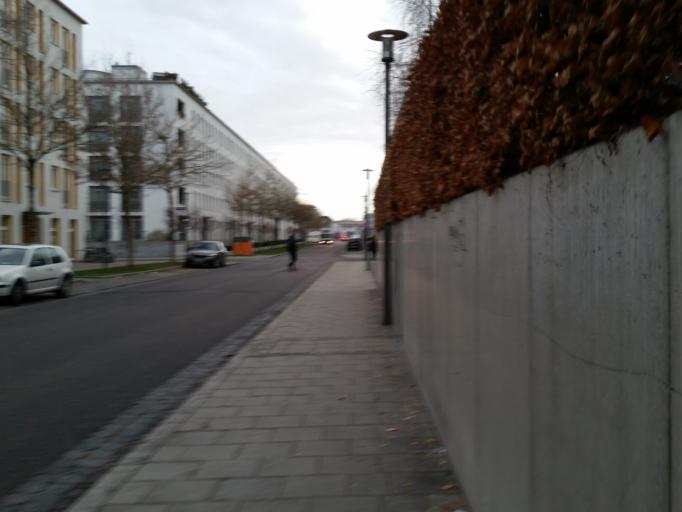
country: DE
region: Bavaria
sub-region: Upper Bavaria
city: Haar
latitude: 48.1309
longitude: 11.6889
